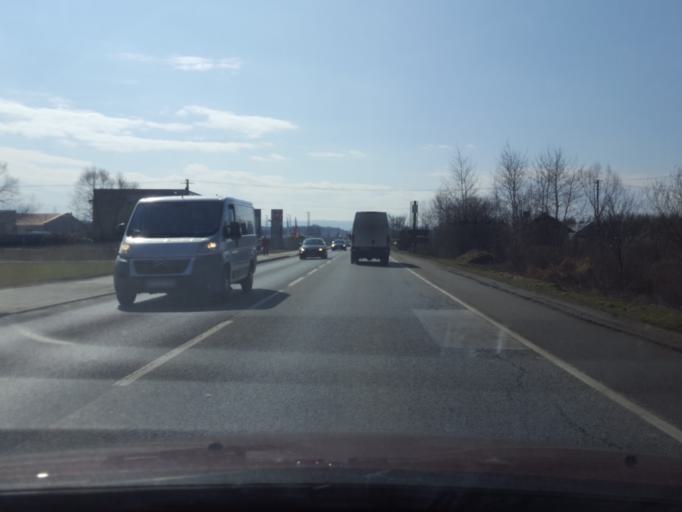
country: PL
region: Lesser Poland Voivodeship
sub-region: Powiat nowosadecki
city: Chelmiec
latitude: 49.6640
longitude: 20.6887
